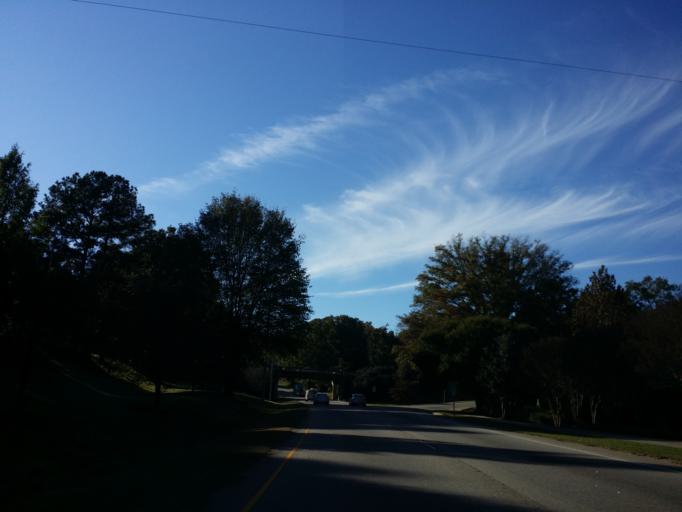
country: US
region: North Carolina
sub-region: Wake County
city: West Raleigh
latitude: 35.7792
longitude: -78.6657
